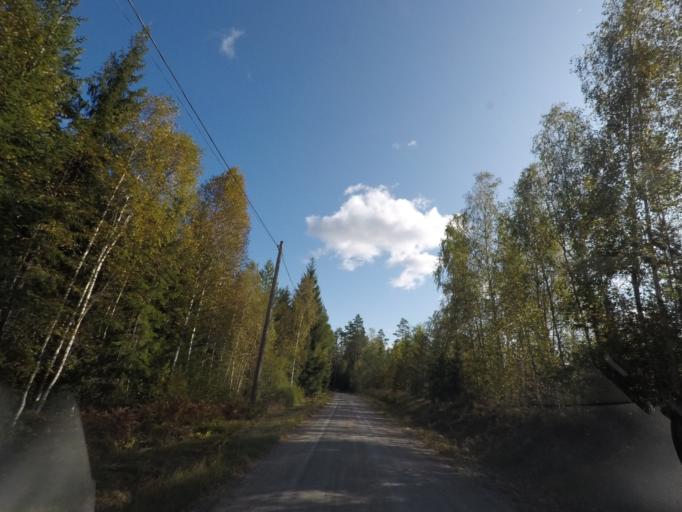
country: SE
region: Vaestmanland
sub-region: Skinnskattebergs Kommun
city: Skinnskatteberg
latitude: 59.8269
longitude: 15.5165
